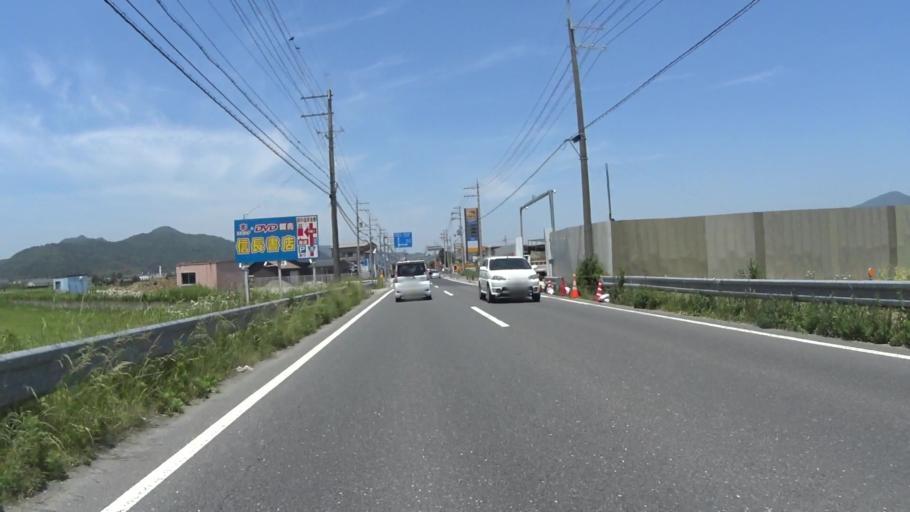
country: JP
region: Kyoto
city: Kameoka
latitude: 35.0203
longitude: 135.5611
